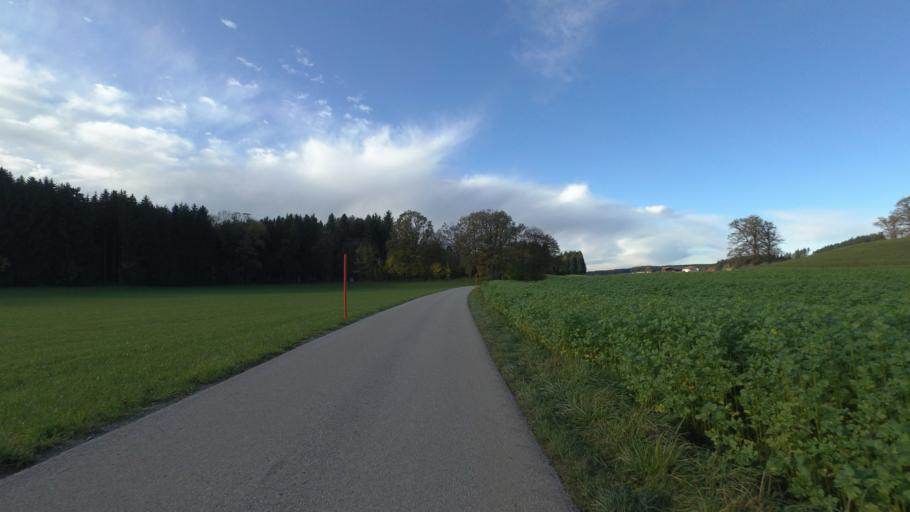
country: DE
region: Bavaria
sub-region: Upper Bavaria
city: Nussdorf
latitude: 47.9255
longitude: 12.5703
